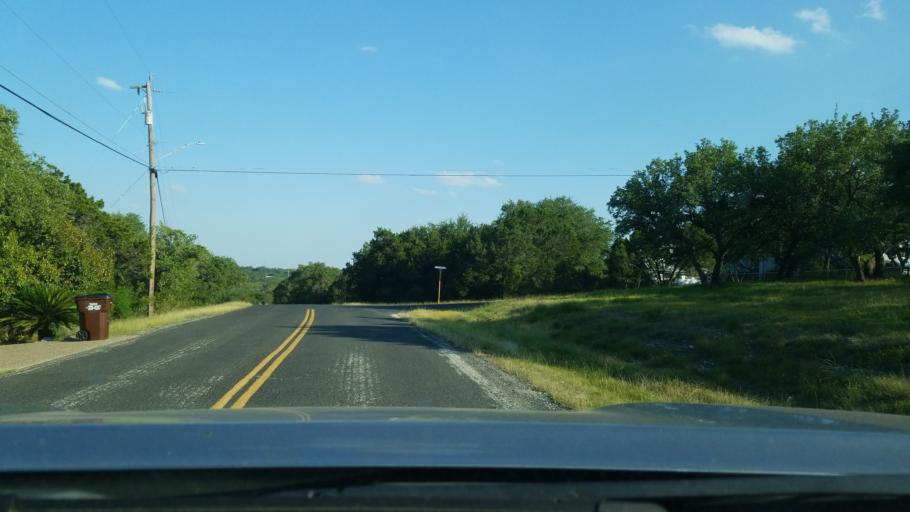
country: US
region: Texas
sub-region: Bexar County
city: Timberwood Park
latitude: 29.7013
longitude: -98.4374
